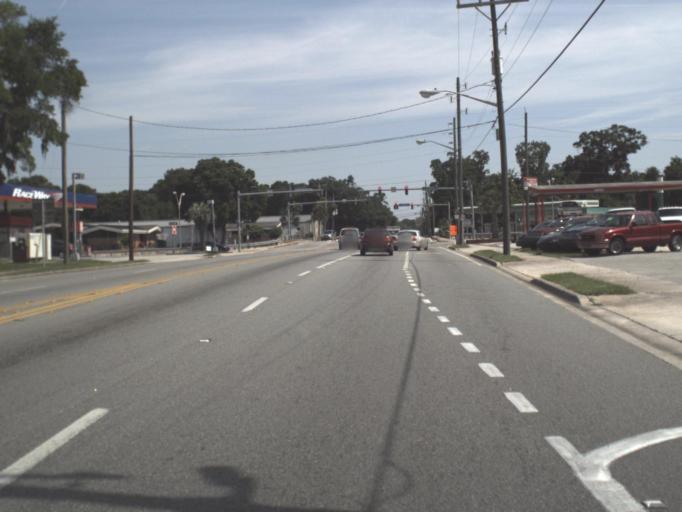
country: US
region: Florida
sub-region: Duval County
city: Jacksonville
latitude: 30.3262
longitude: -81.5969
